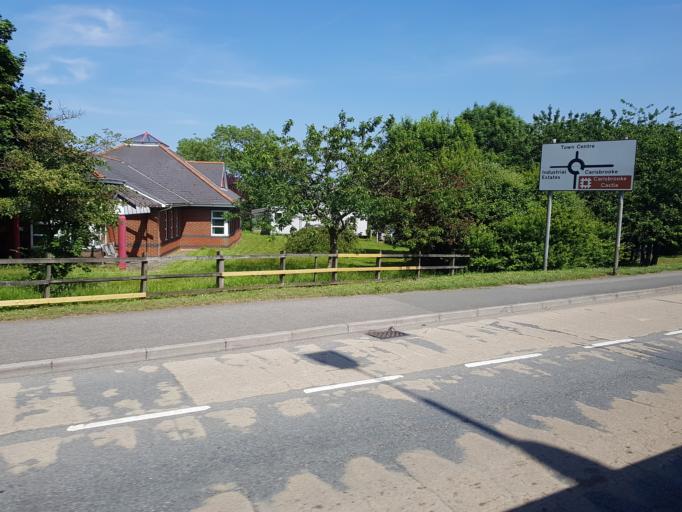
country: GB
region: England
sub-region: Isle of Wight
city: Newport
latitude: 50.7087
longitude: -1.3011
